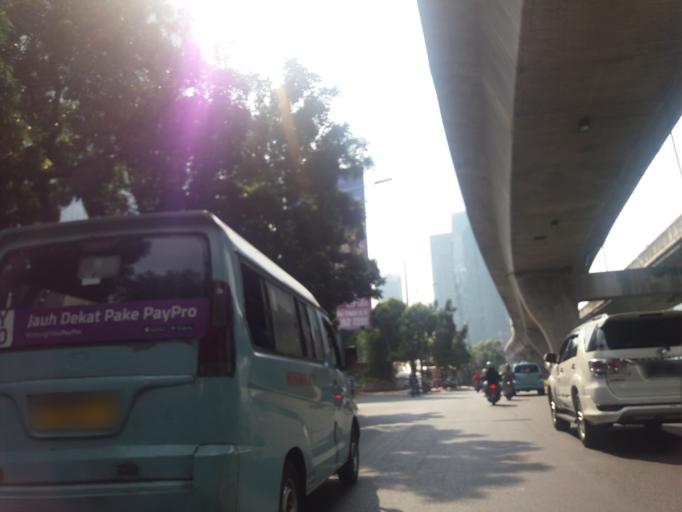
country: ID
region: Jakarta Raya
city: Jakarta
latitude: -6.2218
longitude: 106.8209
